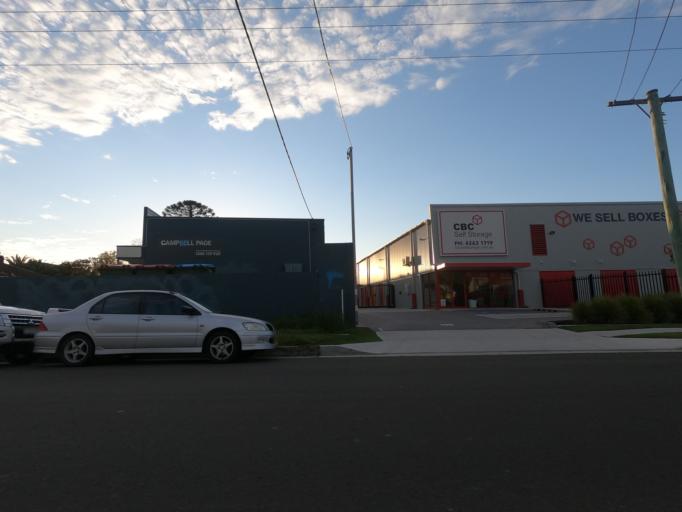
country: AU
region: New South Wales
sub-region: Wollongong
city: Dapto
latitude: -34.4950
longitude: 150.7921
